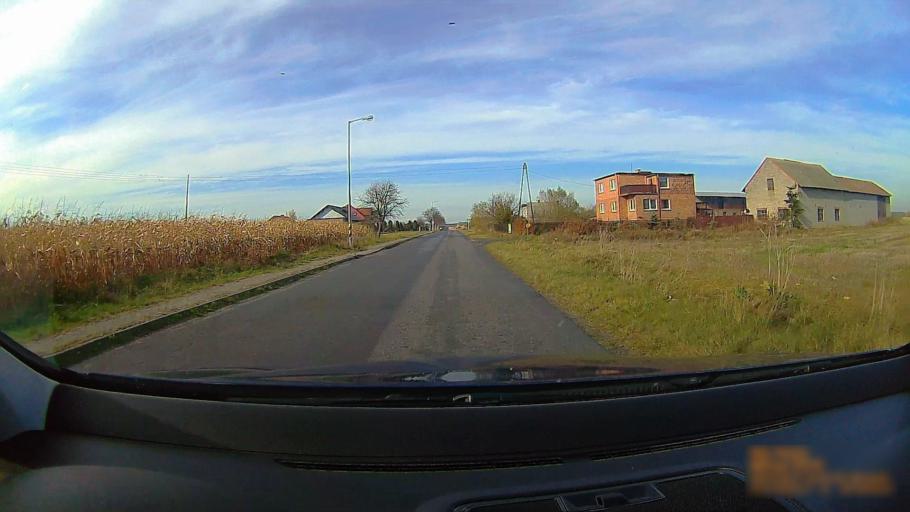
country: PL
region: Greater Poland Voivodeship
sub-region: Powiat ostrzeszowski
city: Doruchow
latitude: 51.4228
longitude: 18.0601
